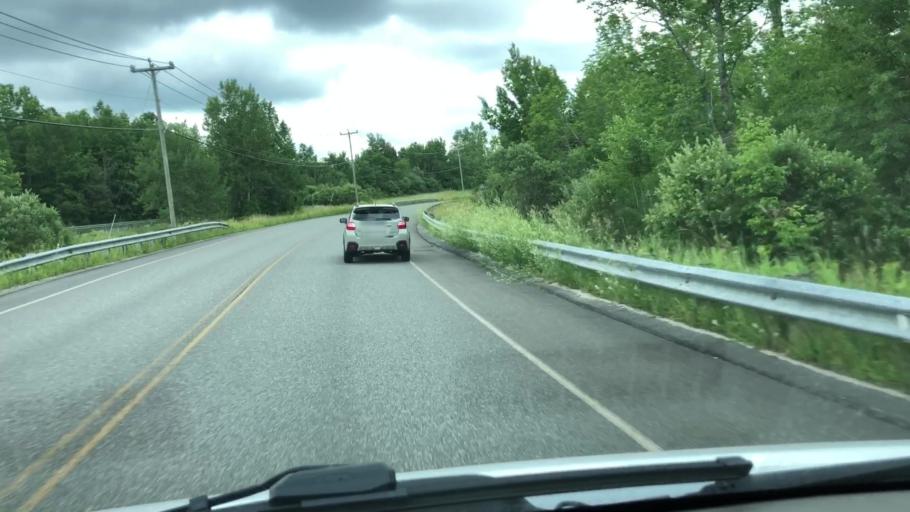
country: US
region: Massachusetts
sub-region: Berkshire County
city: Hinsdale
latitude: 42.5208
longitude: -73.0590
